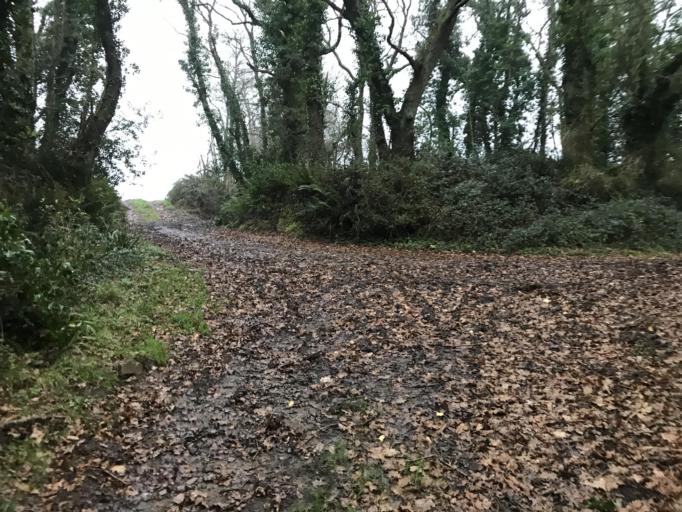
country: FR
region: Brittany
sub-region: Departement du Finistere
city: Logonna-Daoulas
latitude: 48.3247
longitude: -4.2775
